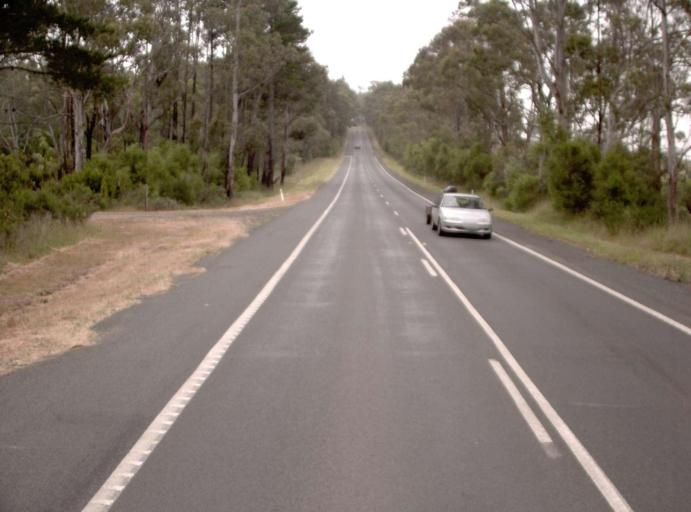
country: AU
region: Victoria
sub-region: Latrobe
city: Moe
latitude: -38.3074
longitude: 146.2733
